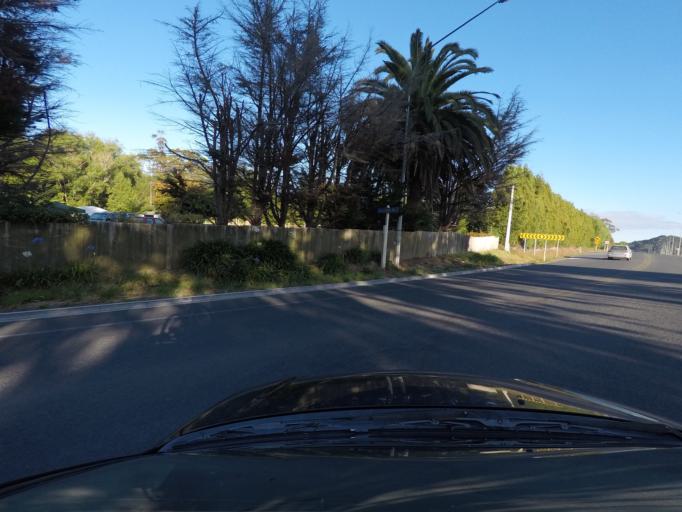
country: NZ
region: Northland
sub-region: Whangarei
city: Whangarei
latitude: -35.6396
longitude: 174.2969
